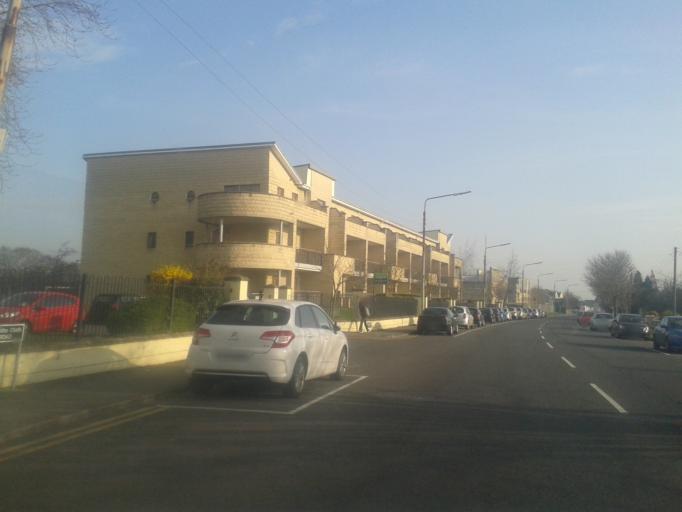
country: IE
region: Leinster
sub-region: Fingal County
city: Swords
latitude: 53.4510
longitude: -6.2256
